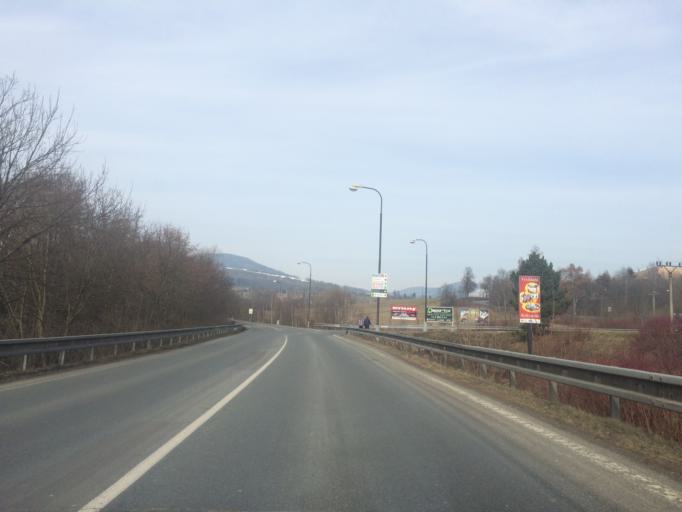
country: CZ
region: Kralovehradecky
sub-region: Okres Trutnov
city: Vrchlabi
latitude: 50.6110
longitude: 15.6037
